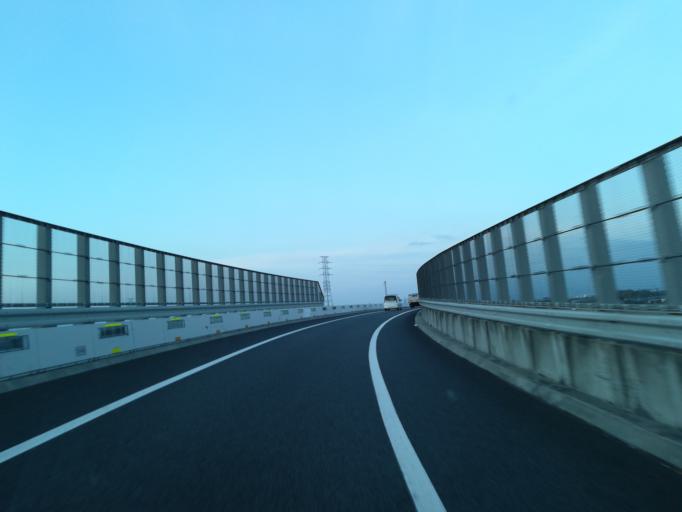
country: JP
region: Gunma
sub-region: Sawa-gun
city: Tamamura
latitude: 36.3204
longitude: 139.0760
